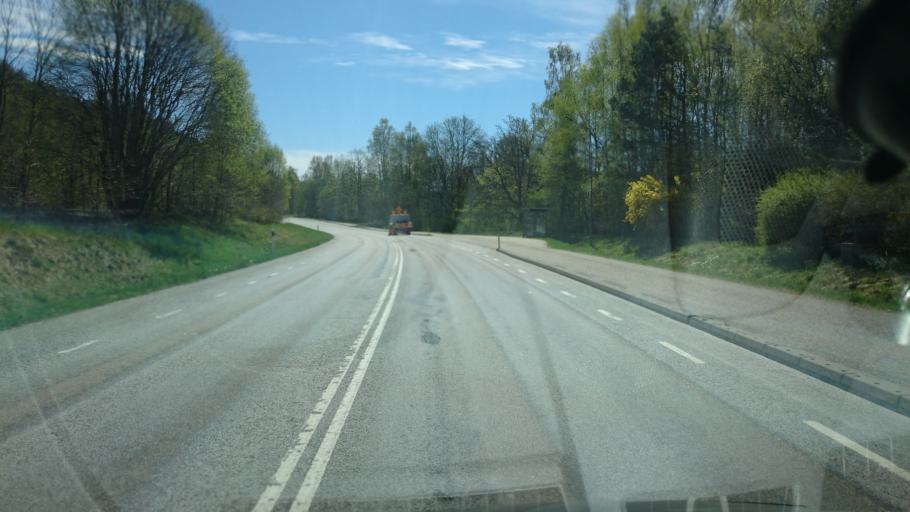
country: SE
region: Vaestra Goetaland
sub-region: Munkedals Kommun
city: Munkedal
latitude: 58.4526
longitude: 11.6898
